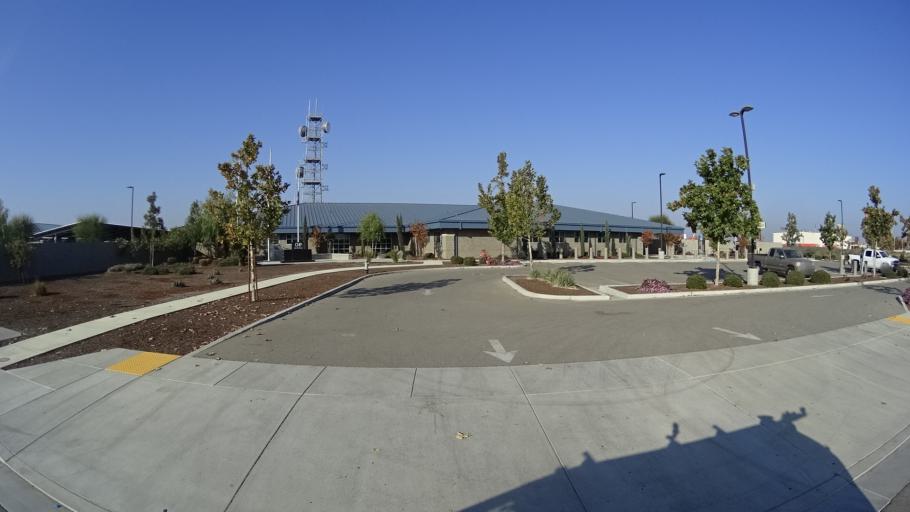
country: US
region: California
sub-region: Kern County
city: Greenfield
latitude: 35.2644
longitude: -119.0251
